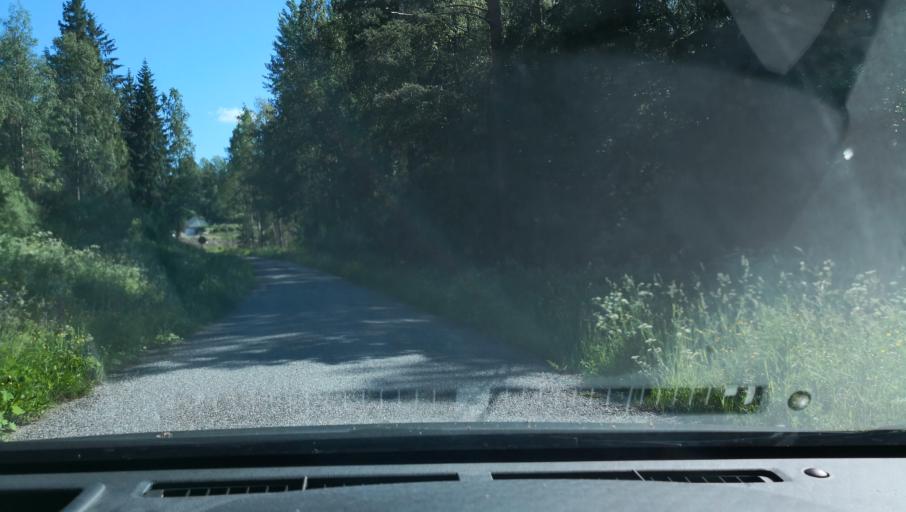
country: SE
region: Soedermanland
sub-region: Eskilstuna Kommun
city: Arla
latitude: 59.3243
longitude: 16.5965
